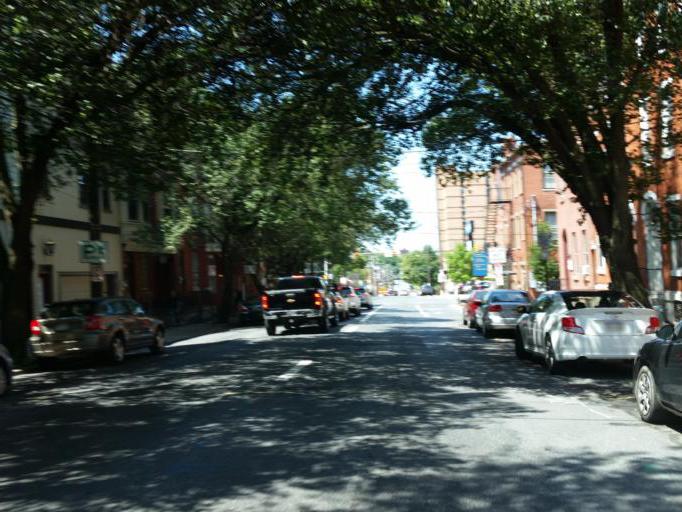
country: US
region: Pennsylvania
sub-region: Lancaster County
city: Lancaster
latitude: 40.0428
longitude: -76.3056
